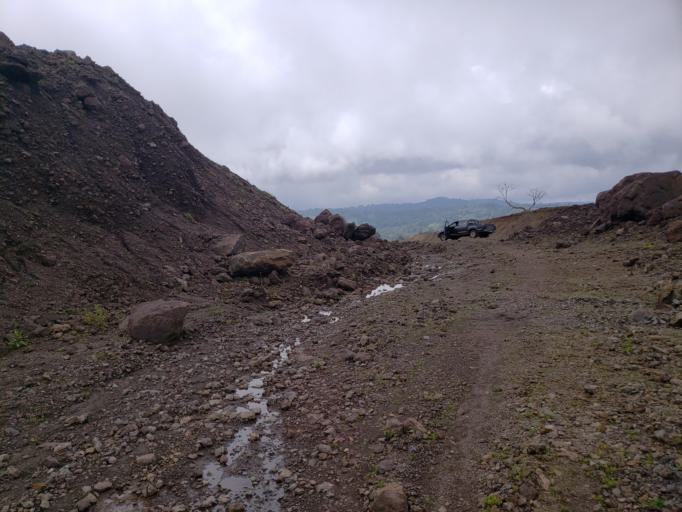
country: ET
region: Oromiya
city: Dodola
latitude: 6.6545
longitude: 39.3624
